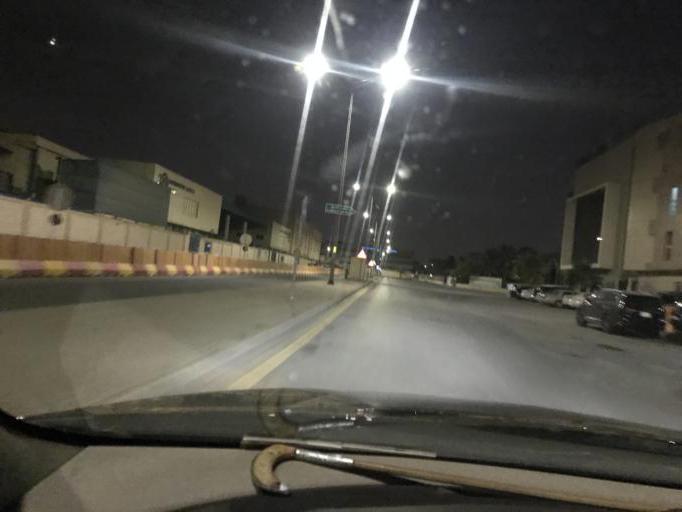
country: SA
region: Ar Riyad
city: Riyadh
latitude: 24.7987
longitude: 46.7087
